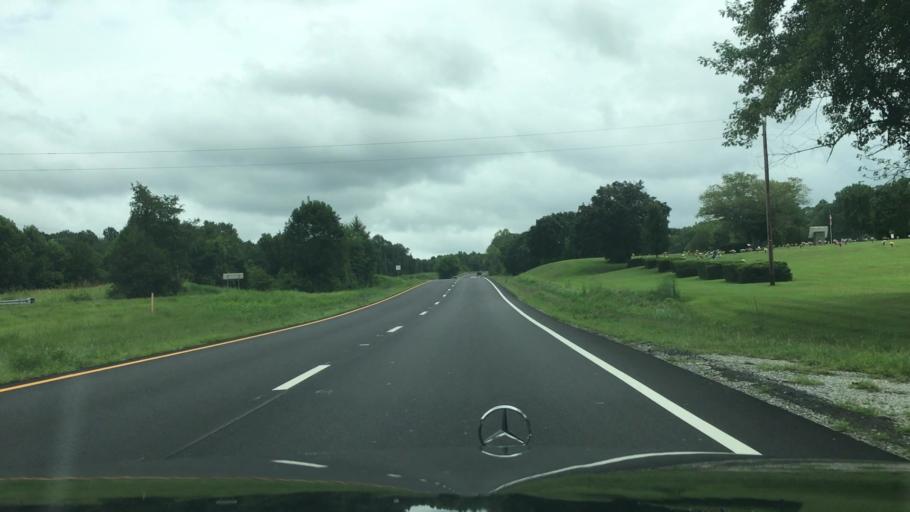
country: US
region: Virginia
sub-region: Prince Edward County
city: Farmville
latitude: 37.2756
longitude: -78.3179
